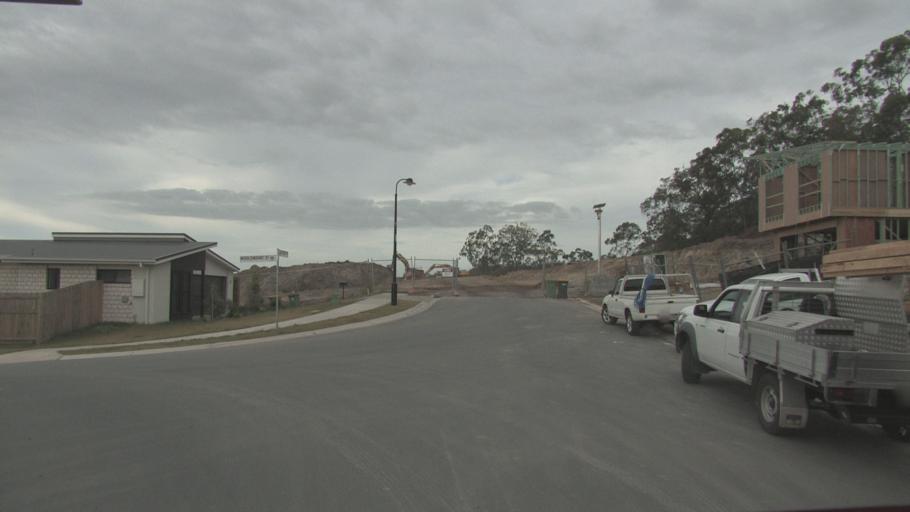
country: AU
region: Queensland
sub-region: Logan
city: Windaroo
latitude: -27.7229
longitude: 153.1649
